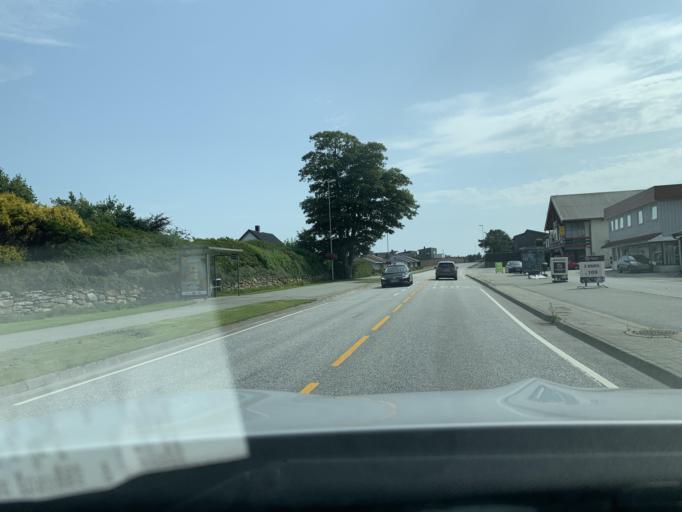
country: NO
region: Rogaland
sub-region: Klepp
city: Kleppe
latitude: 58.7706
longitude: 5.6299
